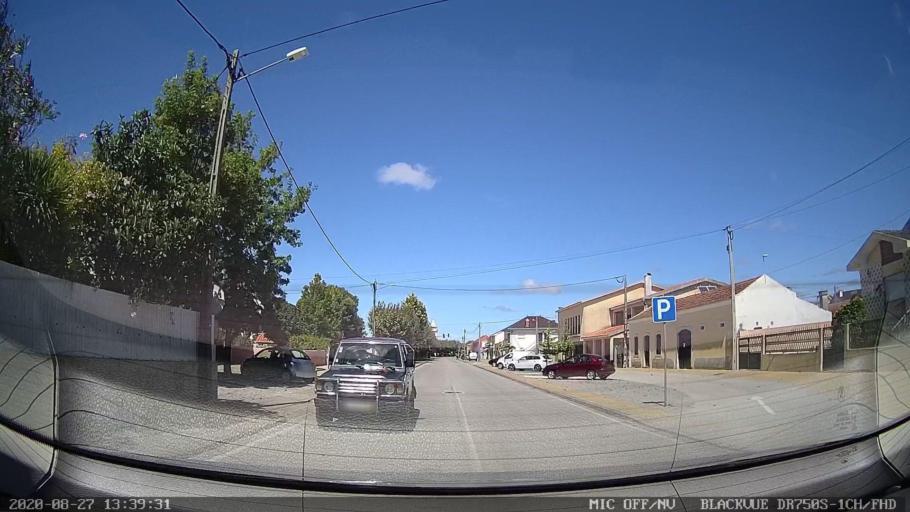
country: PT
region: Coimbra
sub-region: Mira
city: Mira
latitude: 40.4406
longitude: -8.7282
